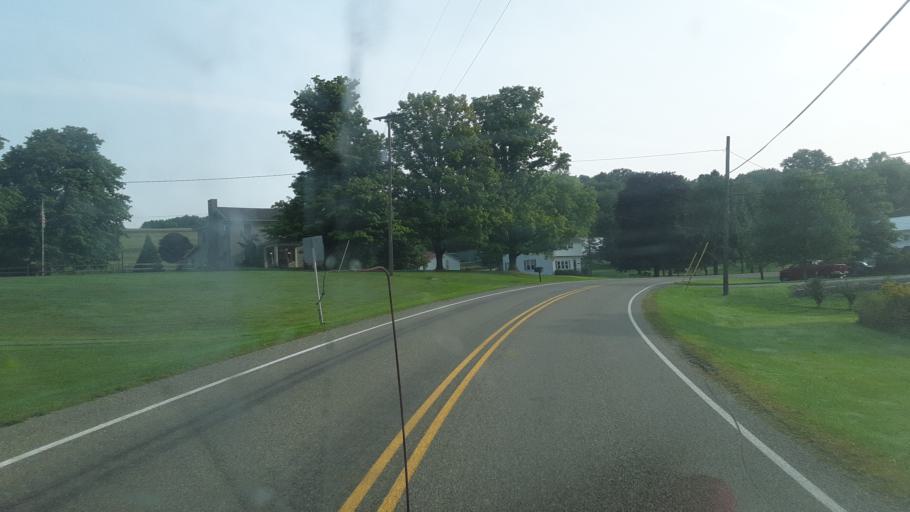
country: US
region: Pennsylvania
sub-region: Jefferson County
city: Punxsutawney
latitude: 40.9638
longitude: -79.0375
